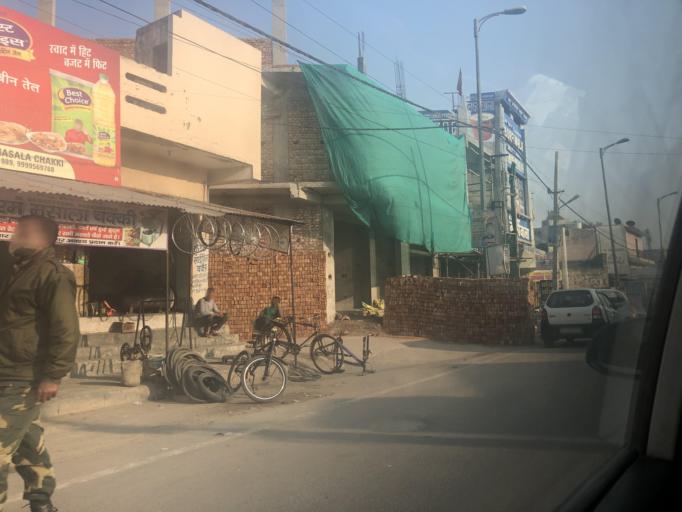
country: IN
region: Haryana
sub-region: Gurgaon
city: Gurgaon
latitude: 28.5589
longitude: 77.0037
